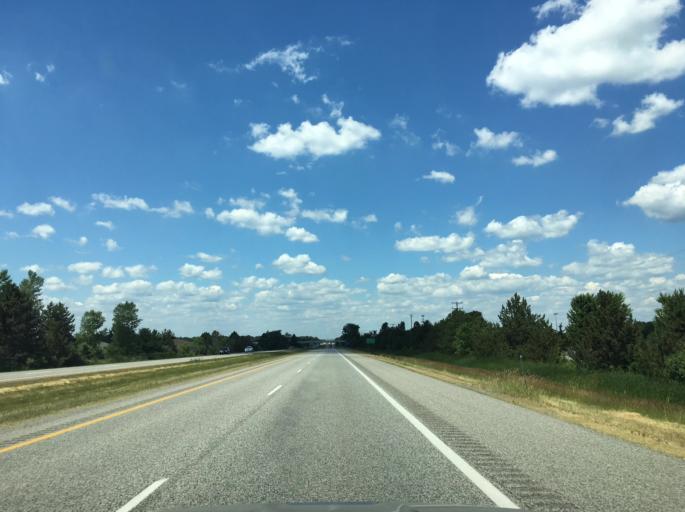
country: US
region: Michigan
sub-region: Midland County
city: Midland
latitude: 43.6560
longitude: -84.2191
